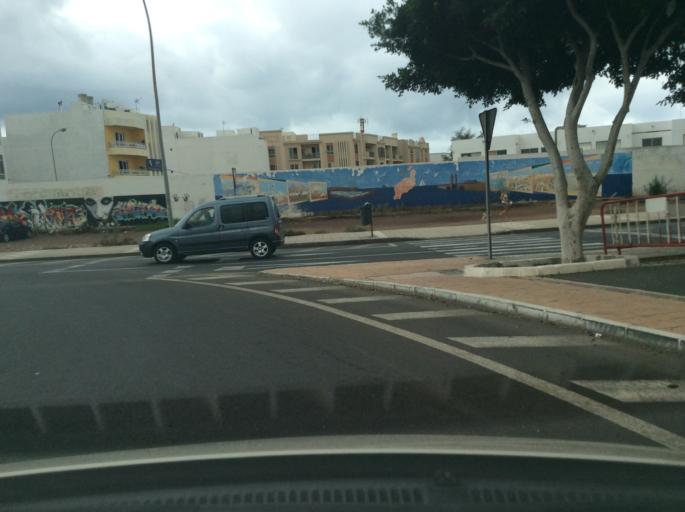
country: ES
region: Canary Islands
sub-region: Provincia de Las Palmas
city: Arrecife
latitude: 28.9674
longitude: -13.5484
